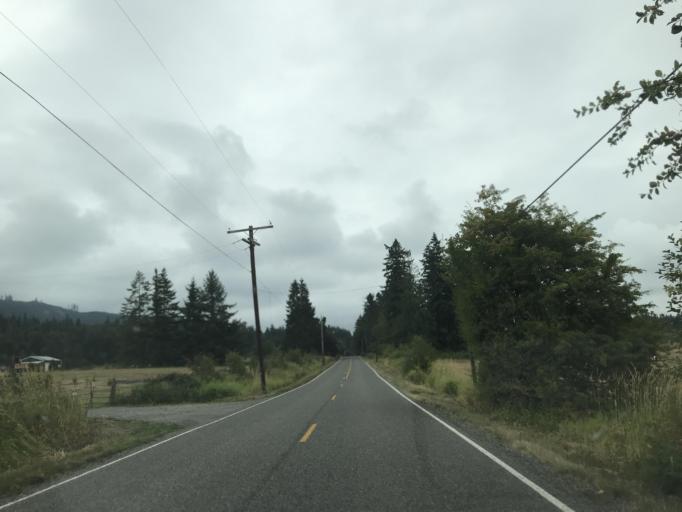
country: US
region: Washington
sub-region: Whatcom County
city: Sudden Valley
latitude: 48.7945
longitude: -122.3330
